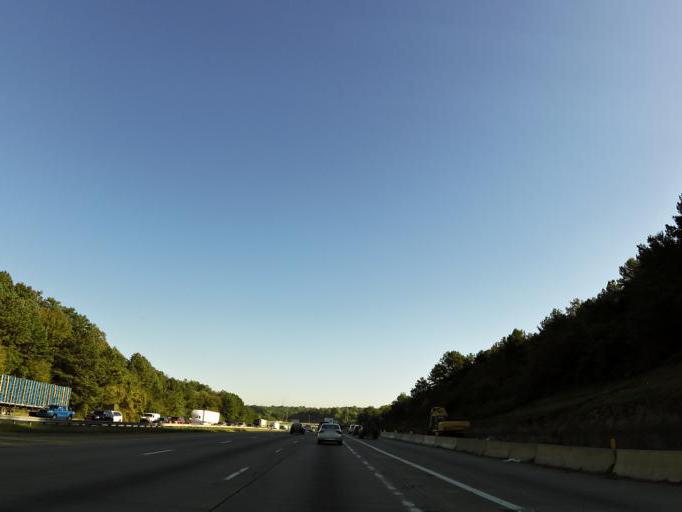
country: US
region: Georgia
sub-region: Cobb County
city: Marietta
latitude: 34.0038
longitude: -84.5644
